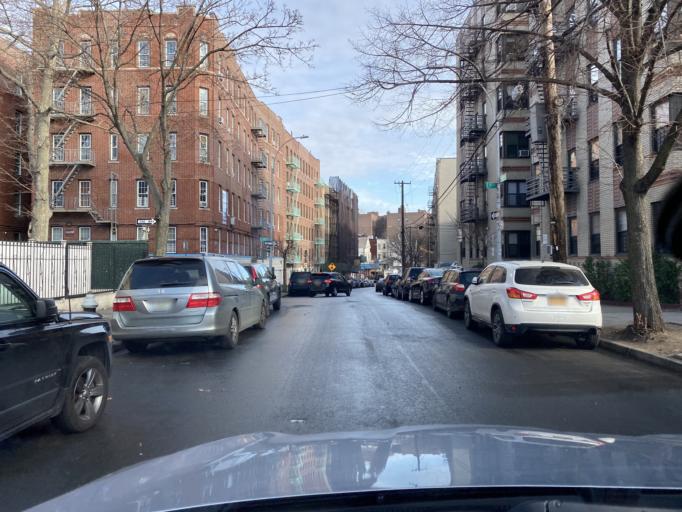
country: US
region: New York
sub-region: Bronx
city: The Bronx
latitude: 40.8679
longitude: -73.8892
